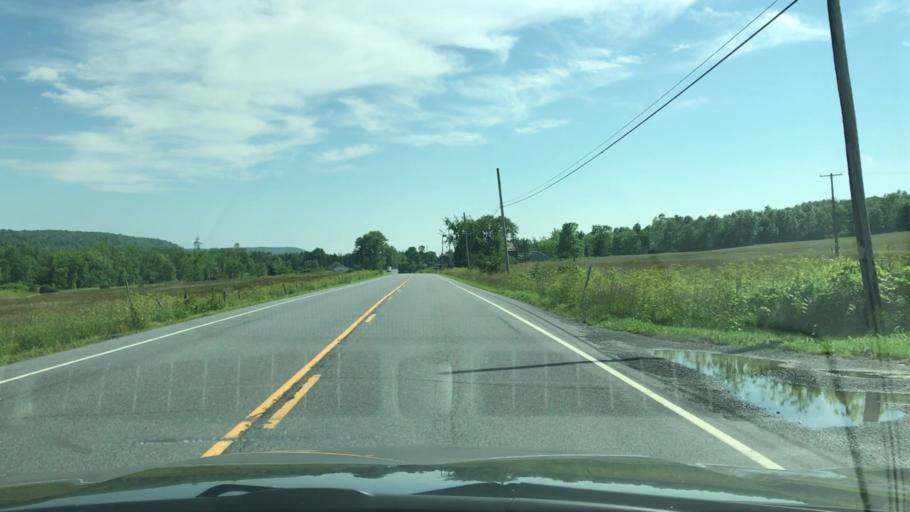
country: US
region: New York
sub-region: Washington County
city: Whitehall
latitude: 43.5160
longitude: -73.4154
